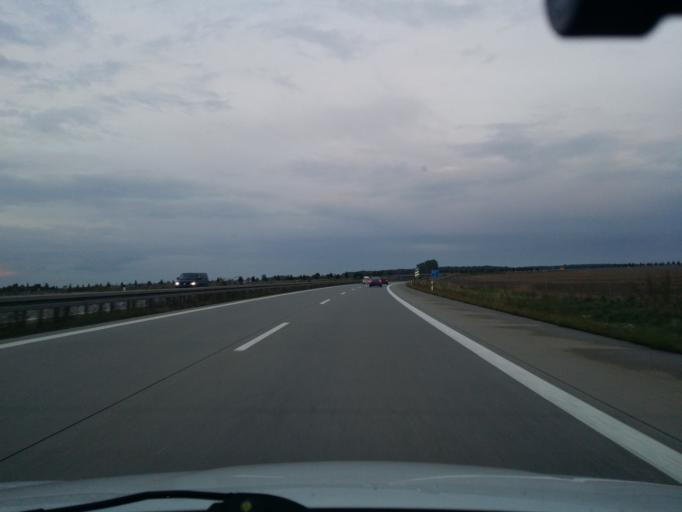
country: DE
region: Saxony
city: Grossposna
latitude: 51.2631
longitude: 12.4558
